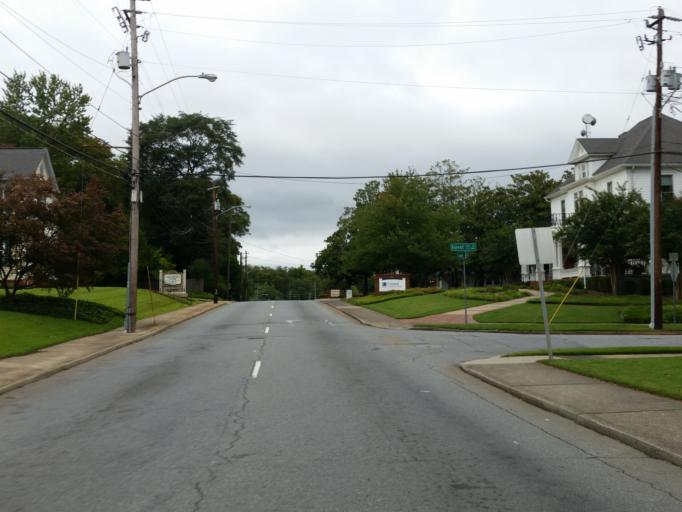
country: US
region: Georgia
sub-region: Cobb County
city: Marietta
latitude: 33.9562
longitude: -84.5491
